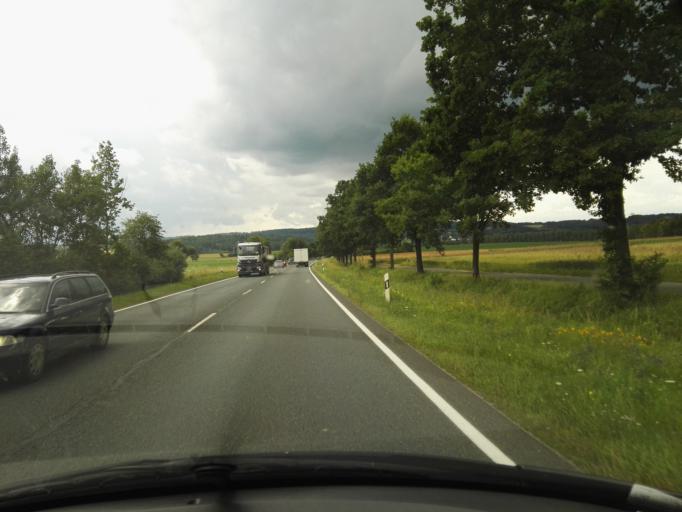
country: DE
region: Bavaria
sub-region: Upper Franconia
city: Hochstadt am Main
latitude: 50.1476
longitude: 11.1604
